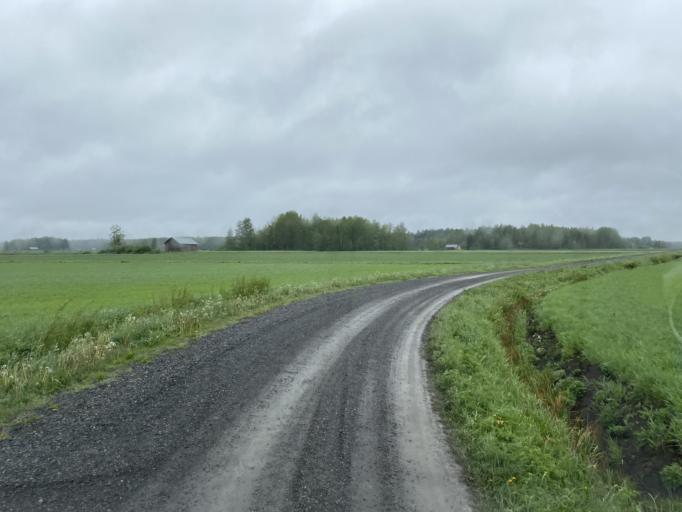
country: FI
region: Pirkanmaa
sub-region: Etelae-Pirkanmaa
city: Urjala
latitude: 60.9613
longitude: 23.5923
